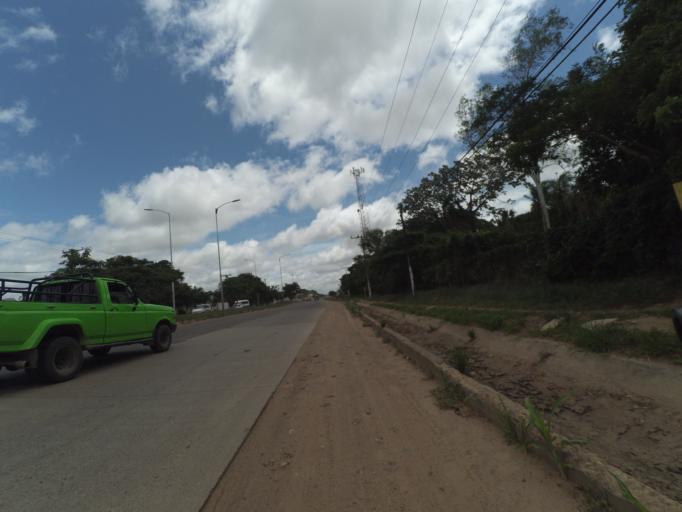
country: BO
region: Santa Cruz
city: Santa Cruz de la Sierra
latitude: -17.8541
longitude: -63.2558
